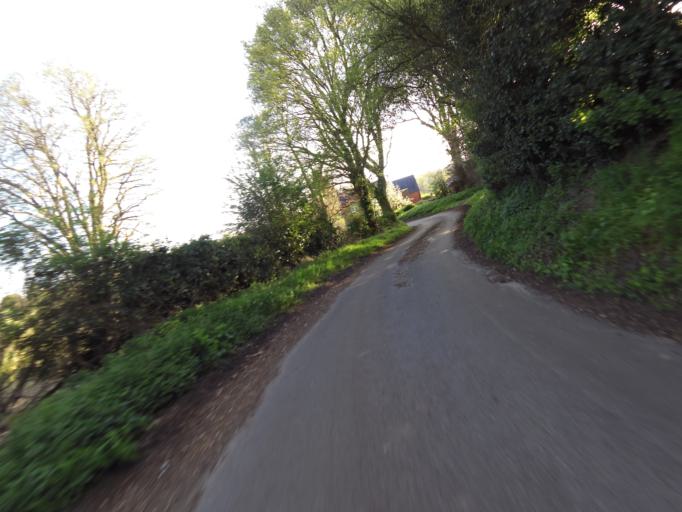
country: GB
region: England
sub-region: Suffolk
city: Bramford
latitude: 52.0403
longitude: 1.0729
